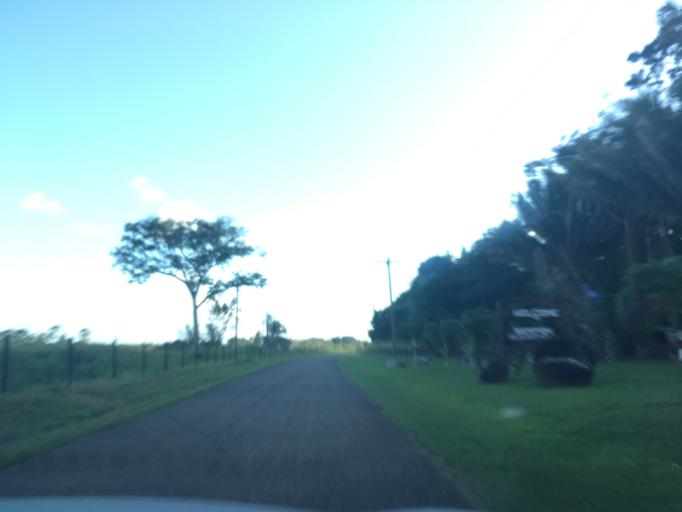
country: BZ
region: Stann Creek
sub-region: Dangriga
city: Dangriga
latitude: 16.8269
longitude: -88.3444
